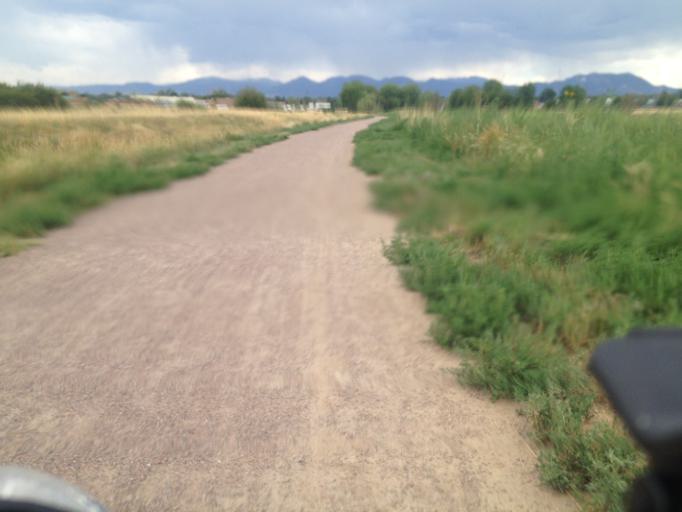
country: US
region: Colorado
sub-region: Boulder County
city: Louisville
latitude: 39.9823
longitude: -105.1194
